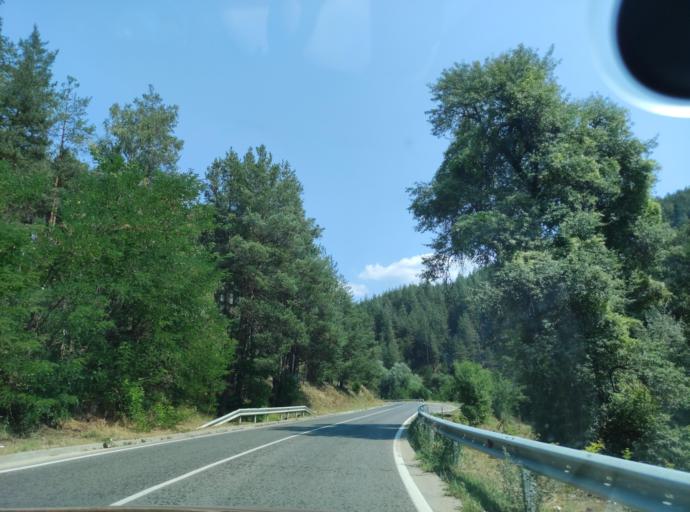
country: BG
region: Blagoevgrad
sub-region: Obshtina Razlog
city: Razlog
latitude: 41.8911
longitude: 23.5336
